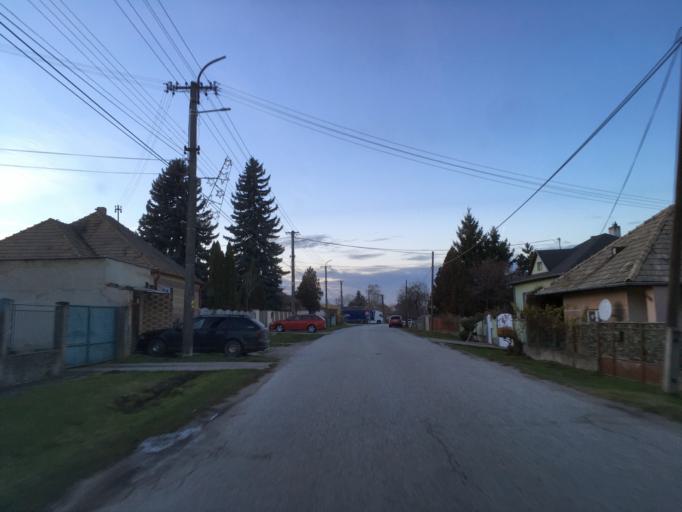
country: SK
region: Nitriansky
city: Svodin
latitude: 47.8695
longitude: 18.4636
